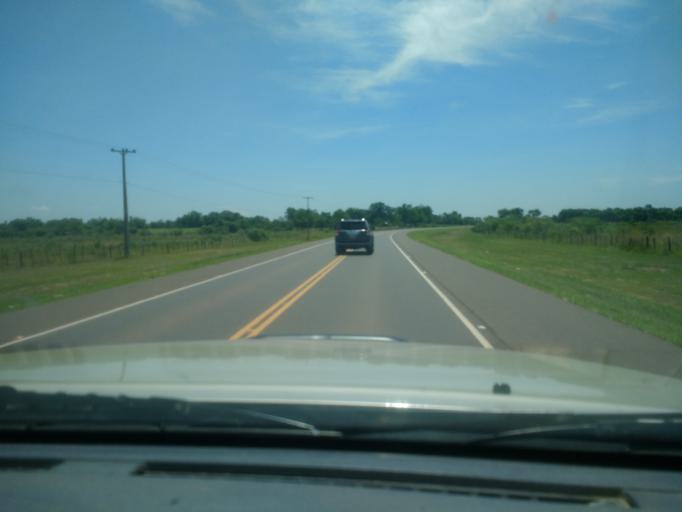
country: PY
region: San Pedro
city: Union
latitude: -24.7166
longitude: -56.5356
